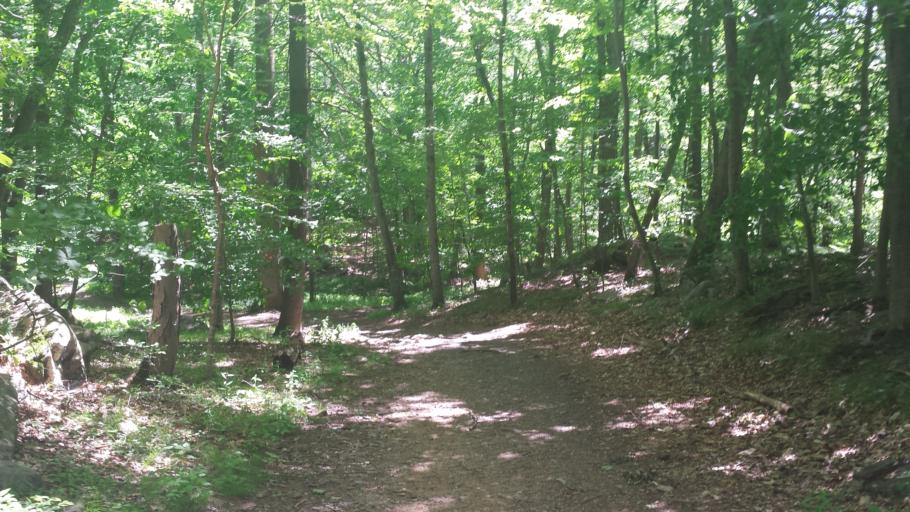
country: US
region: New York
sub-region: Westchester County
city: Pound Ridge
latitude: 41.2426
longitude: -73.5959
